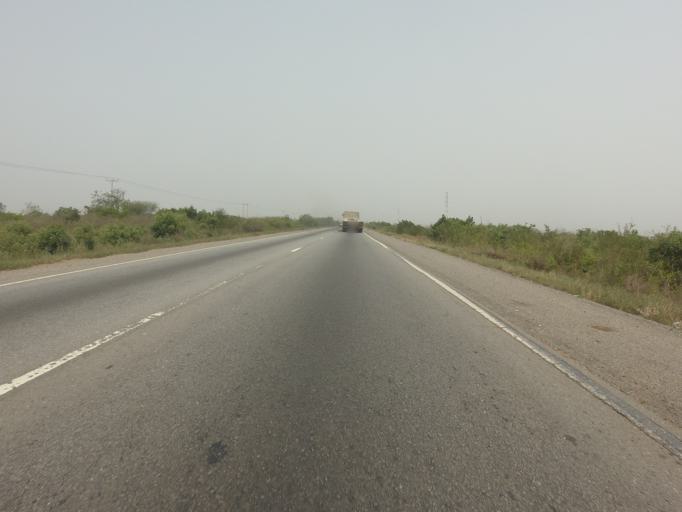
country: GH
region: Greater Accra
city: Tema
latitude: 5.7836
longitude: 0.0997
